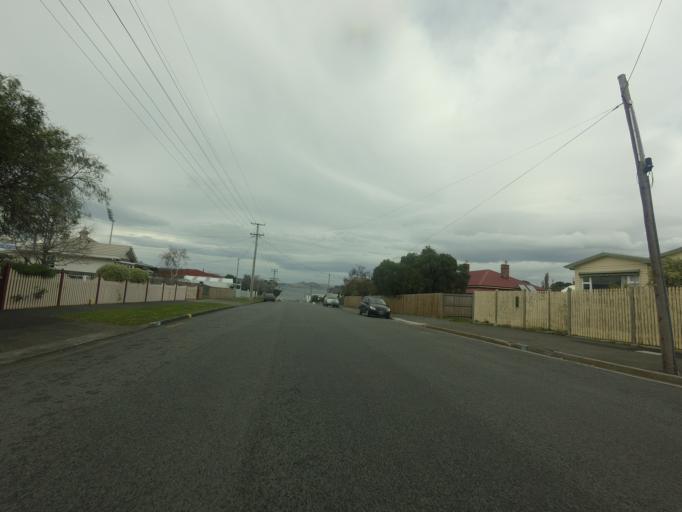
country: AU
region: Tasmania
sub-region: Clarence
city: Bellerive
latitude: -42.8774
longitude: 147.3697
